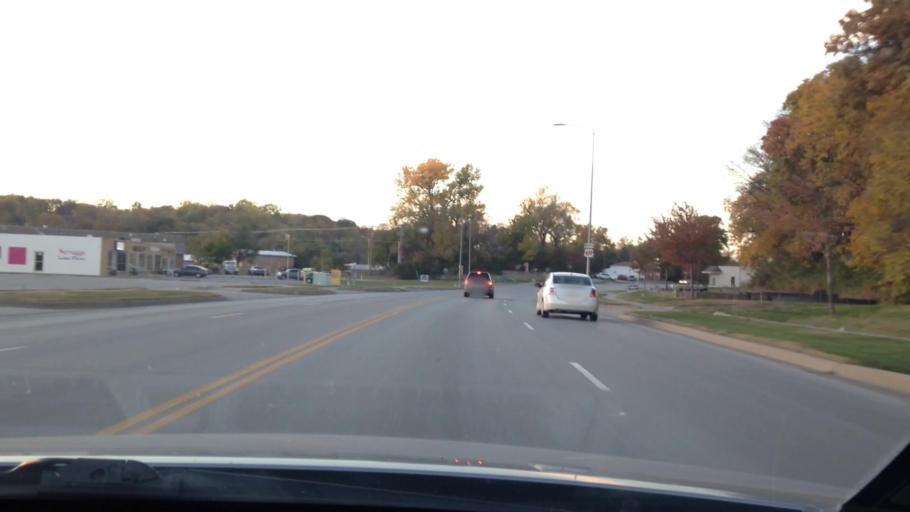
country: US
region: Missouri
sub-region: Platte County
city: Riverside
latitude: 39.1711
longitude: -94.6115
